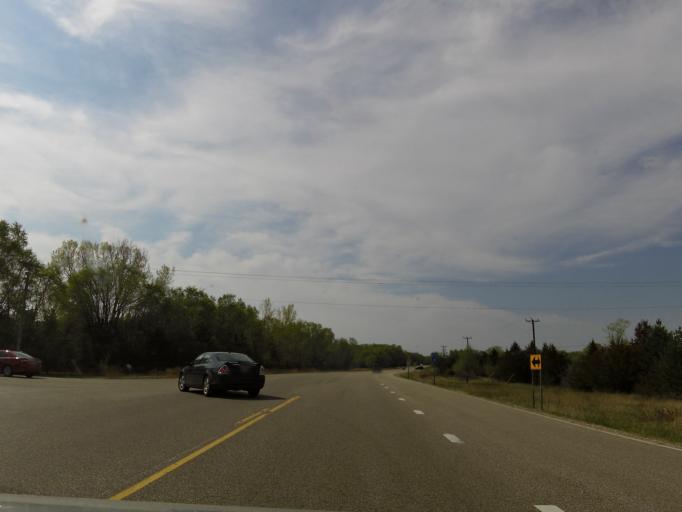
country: US
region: Minnesota
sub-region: Washington County
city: Lake Saint Croix Beach
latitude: 44.9295
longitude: -92.7711
